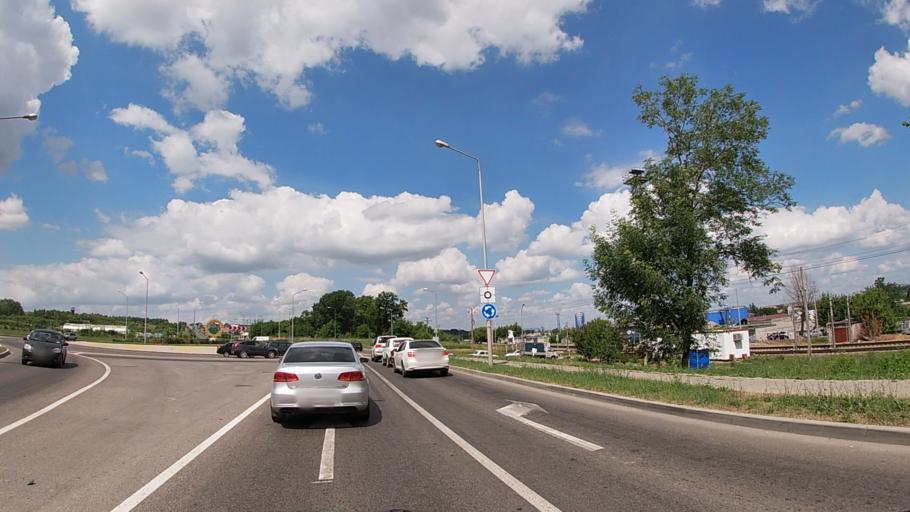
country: RU
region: Belgorod
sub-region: Belgorodskiy Rayon
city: Belgorod
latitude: 50.5950
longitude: 36.5531
